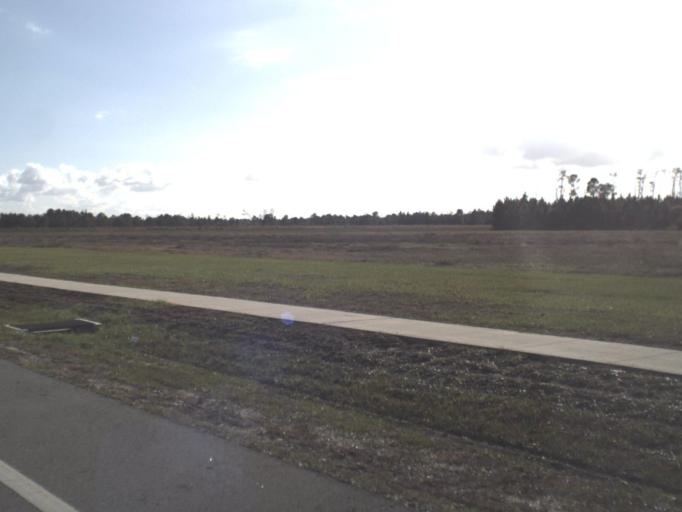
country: US
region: Florida
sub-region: Volusia County
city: Holly Hill
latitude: 29.2195
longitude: -81.0923
